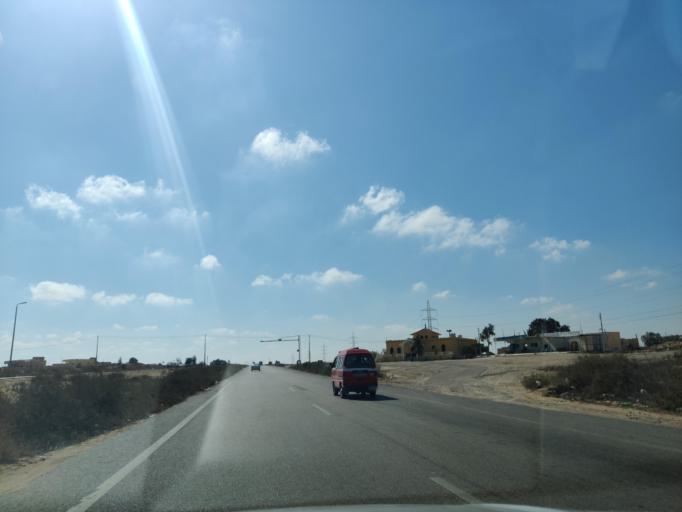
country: EG
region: Muhafazat Matruh
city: Al `Alamayn
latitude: 31.0451
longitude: 28.3448
